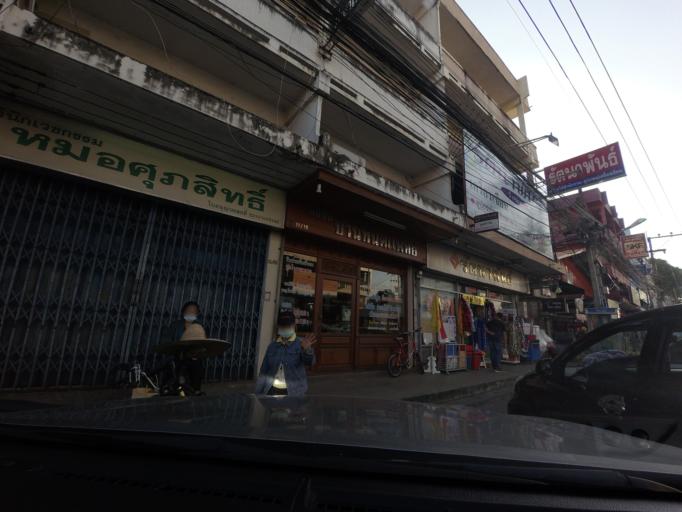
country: TH
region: Lampang
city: Lampang
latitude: 18.2893
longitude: 99.4865
